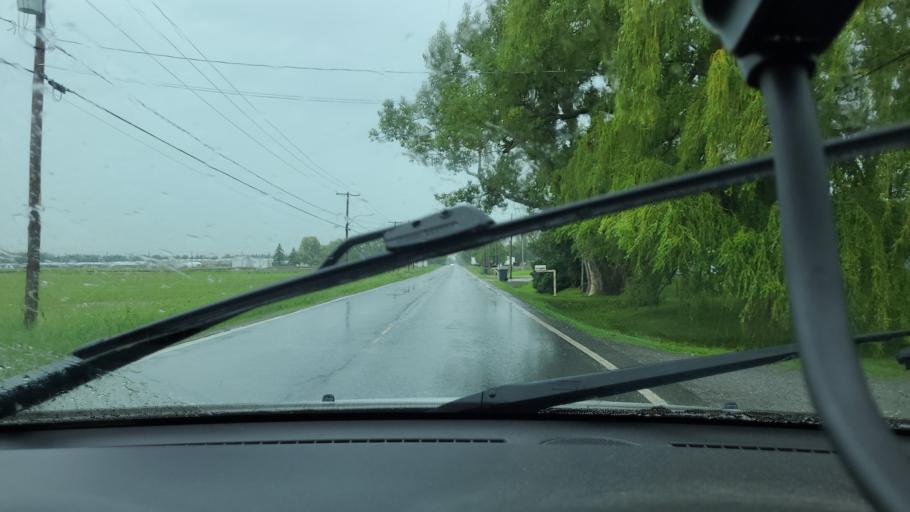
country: CA
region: Quebec
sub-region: Monteregie
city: Saint-Hyacinthe
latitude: 45.6168
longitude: -73.0191
